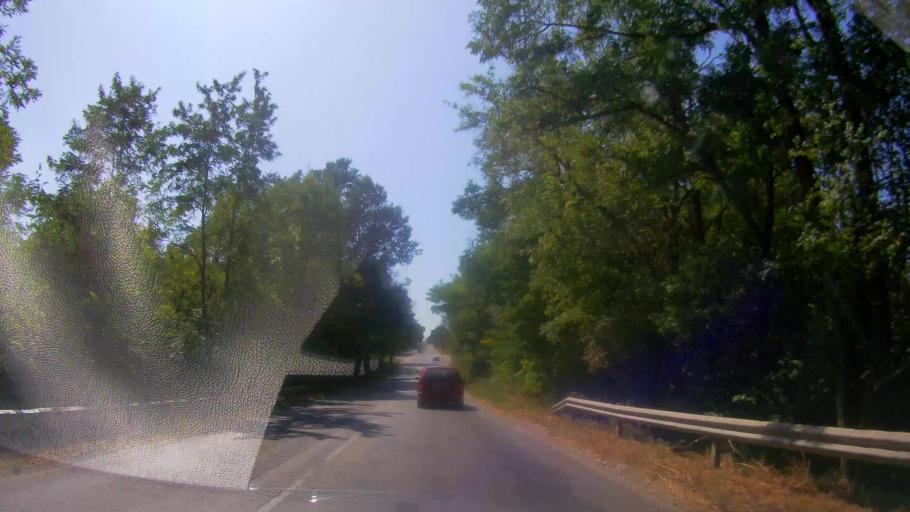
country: BG
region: Veliko Turnovo
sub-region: Obshtina Gorna Oryakhovitsa
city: Purvomaytsi
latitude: 43.2419
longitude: 25.6427
